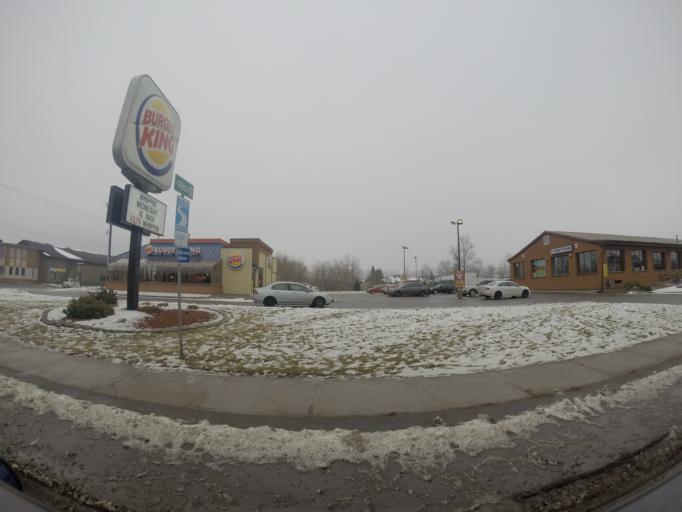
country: CA
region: Ontario
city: Greater Sudbury
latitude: 46.5074
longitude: -80.9866
